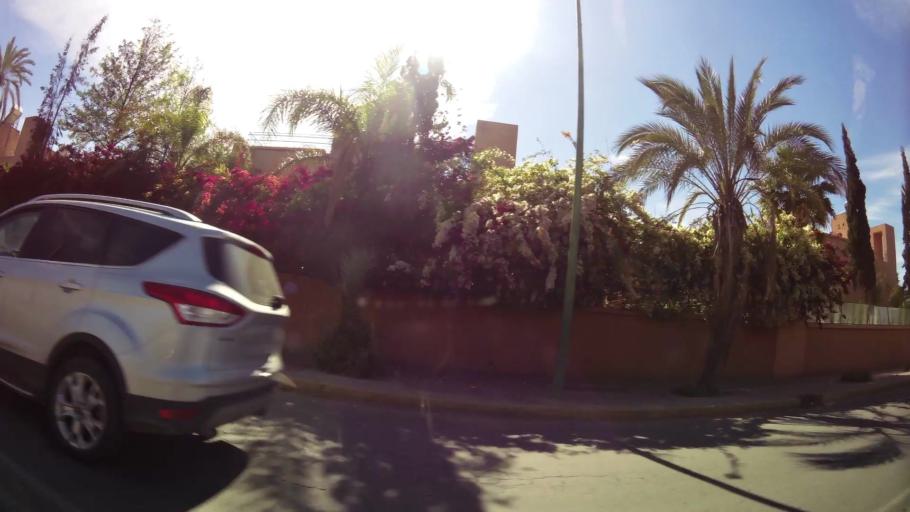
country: MA
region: Marrakech-Tensift-Al Haouz
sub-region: Marrakech
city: Marrakesh
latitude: 31.6583
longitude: -8.0540
